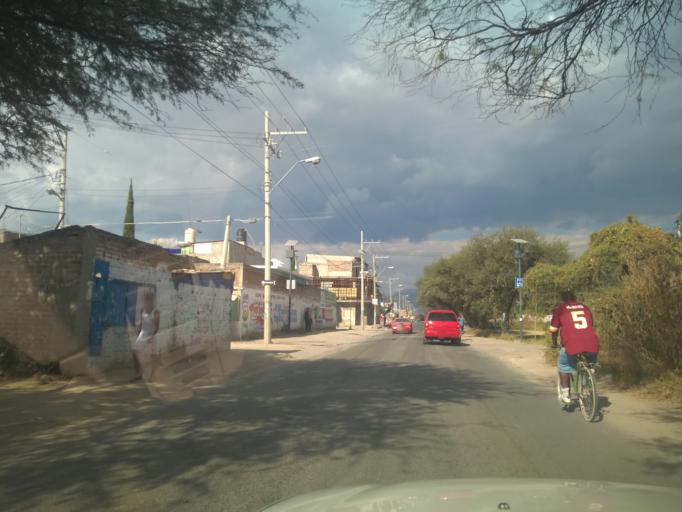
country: MX
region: Guanajuato
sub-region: Leon
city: San Jose de Duran (Los Troncoso)
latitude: 21.0654
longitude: -101.6252
